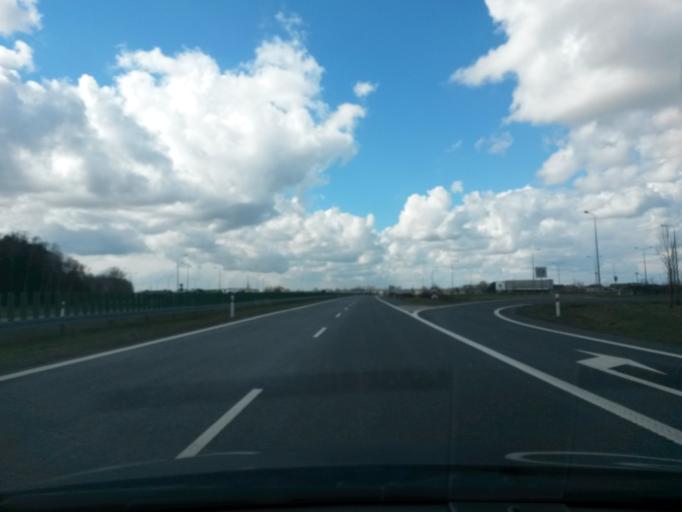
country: PL
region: Lodz Voivodeship
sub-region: Powiat leczycki
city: Swinice Warckie
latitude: 52.0340
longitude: 18.8810
